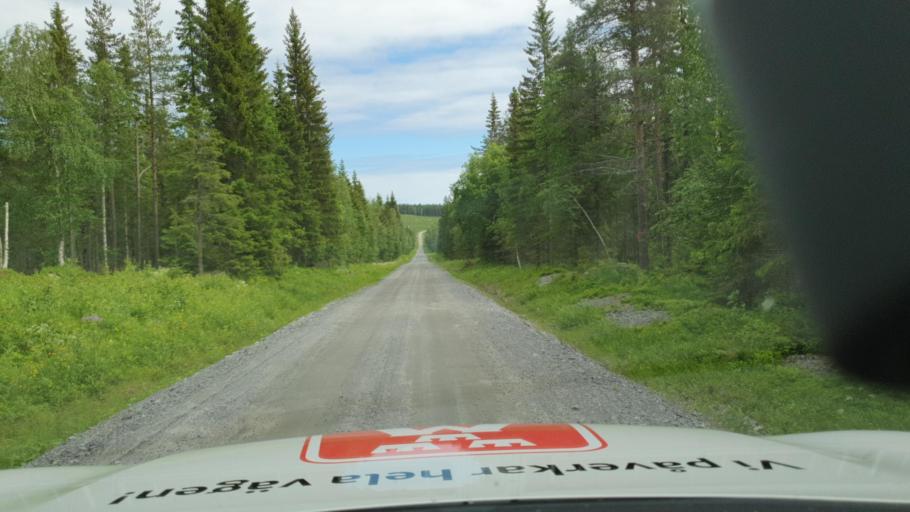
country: SE
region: Vaesterbotten
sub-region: Skelleftea Kommun
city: Langsele
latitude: 64.6397
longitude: 20.2686
